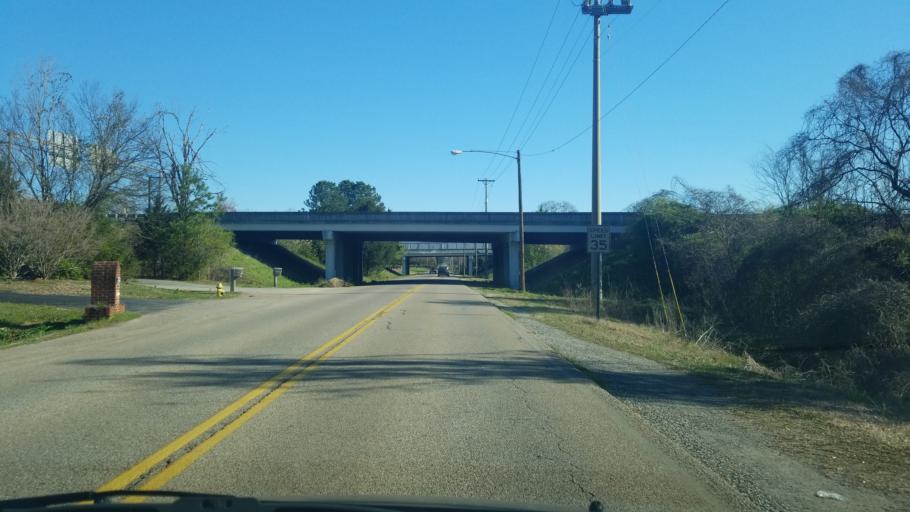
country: US
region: Tennessee
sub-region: Hamilton County
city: East Brainerd
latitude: 35.0270
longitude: -85.1767
